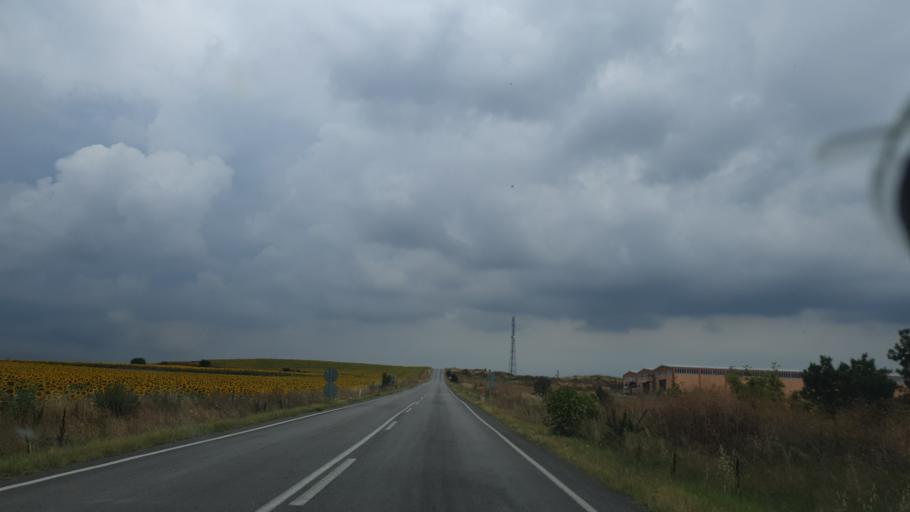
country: TR
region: Tekirdag
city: Hayrabolu
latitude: 41.2235
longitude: 27.0433
